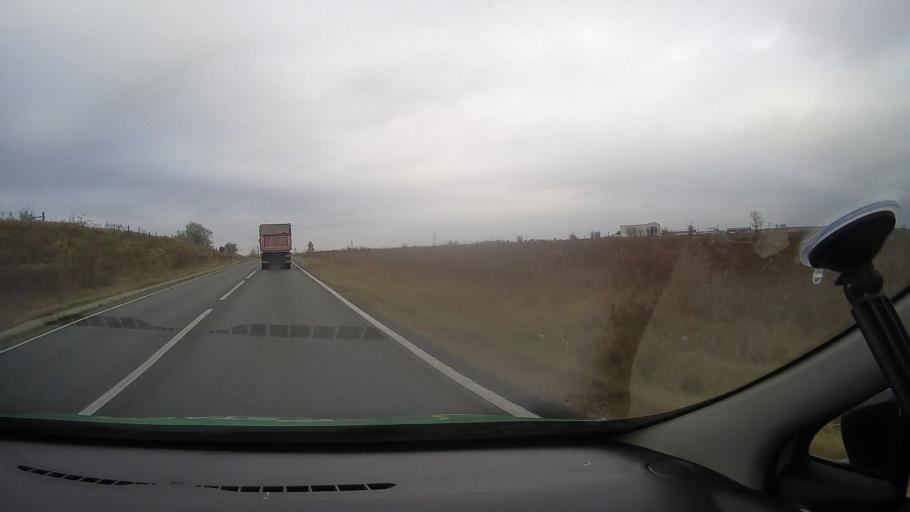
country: RO
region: Constanta
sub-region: Comuna Poarta Alba
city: Poarta Alba
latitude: 44.2284
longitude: 28.3802
